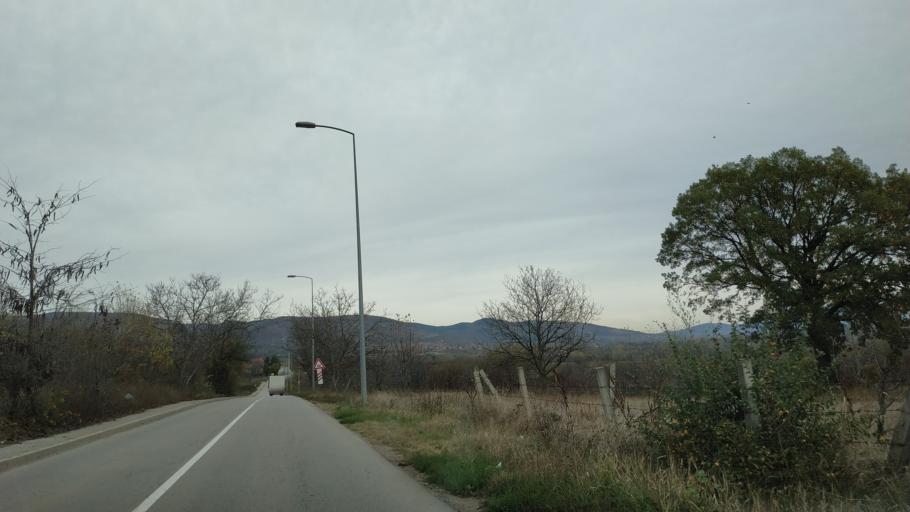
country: RS
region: Central Serbia
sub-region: Nisavski Okrug
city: Nis
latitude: 43.3502
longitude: 21.9397
